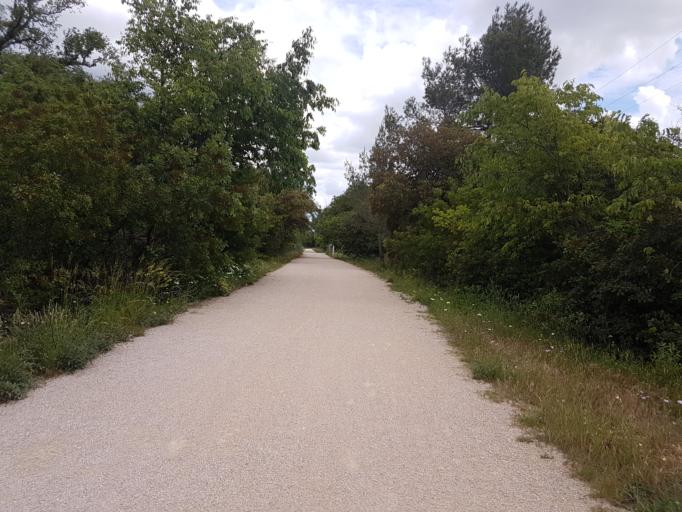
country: FR
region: Languedoc-Roussillon
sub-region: Departement du Gard
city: Vallabregues
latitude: 43.8273
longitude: 4.6223
